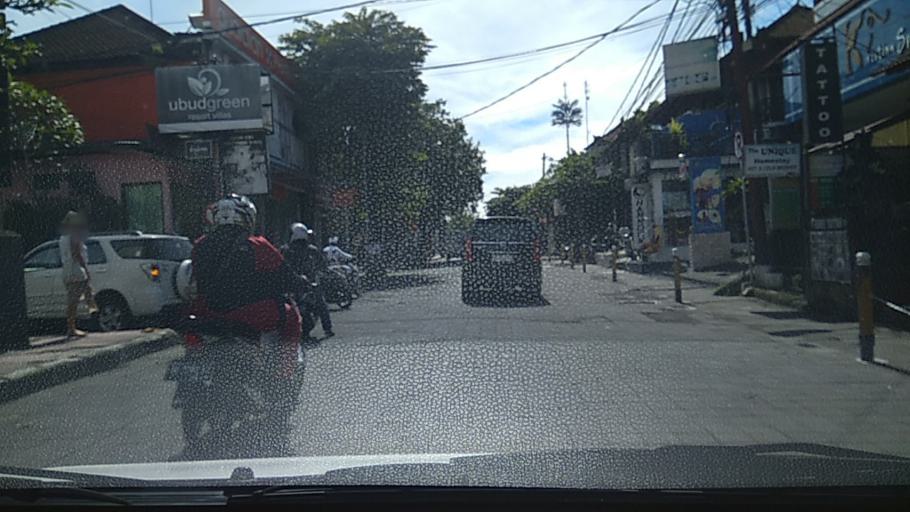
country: ID
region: Bali
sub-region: Kabupaten Gianyar
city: Ubud
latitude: -8.5080
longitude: 115.2649
